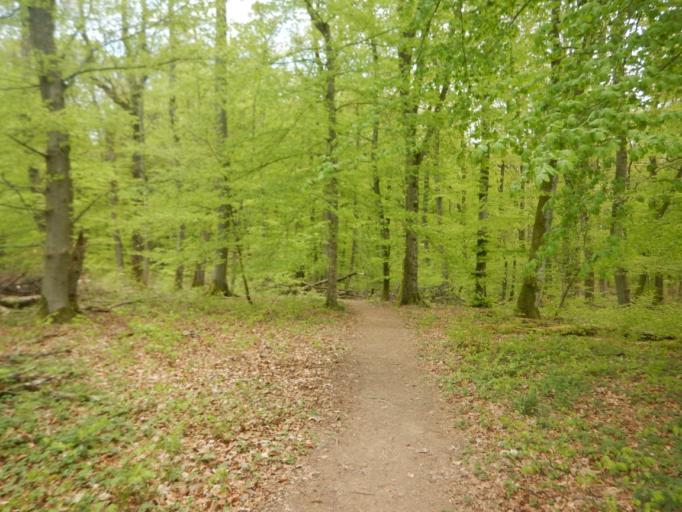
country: LU
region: Grevenmacher
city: Gonderange
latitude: 49.6860
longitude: 6.2610
